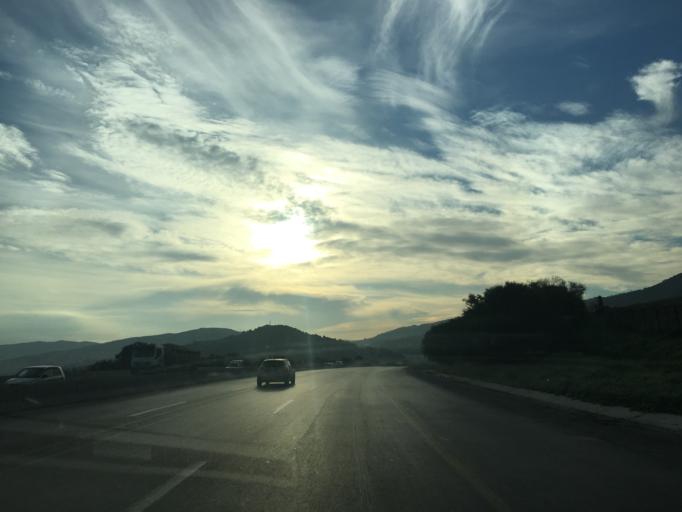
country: DZ
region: Bouira
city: Draa el Mizan
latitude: 36.4708
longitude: 3.7633
